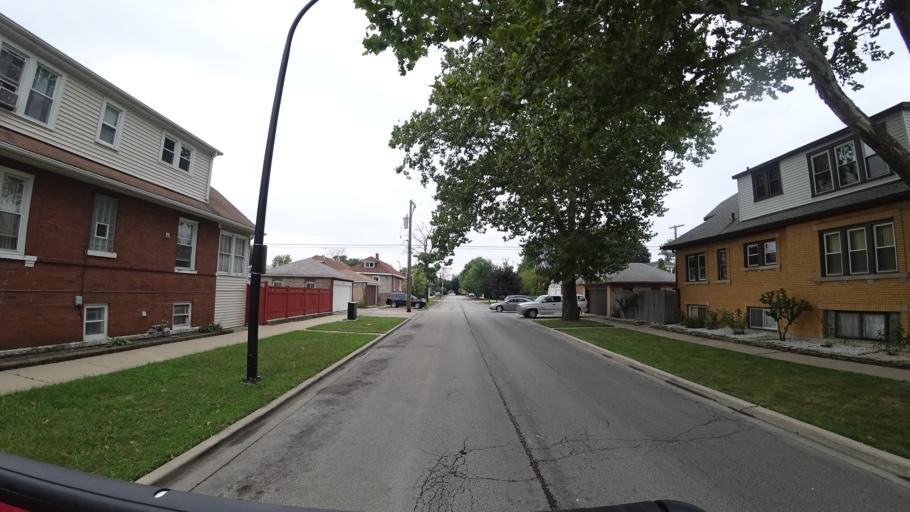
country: US
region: Illinois
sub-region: Cook County
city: Cicero
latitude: 41.8545
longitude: -87.7716
